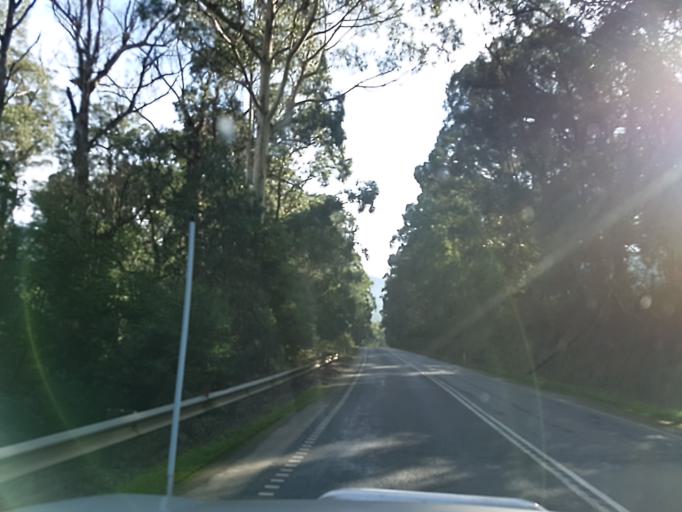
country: AU
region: Victoria
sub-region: Yarra Ranges
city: Yarra Glen
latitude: -37.5017
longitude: 145.4226
